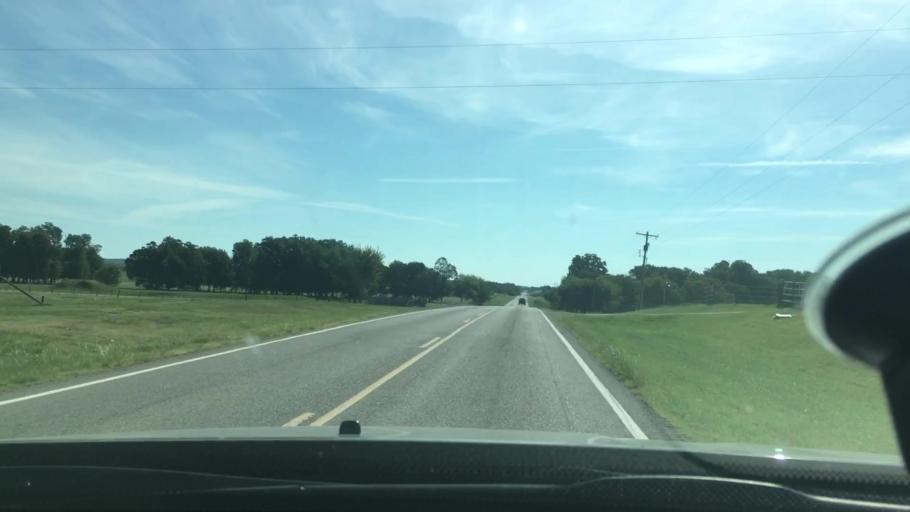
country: US
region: Oklahoma
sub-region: Carter County
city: Ardmore
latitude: 34.3327
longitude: -97.1739
